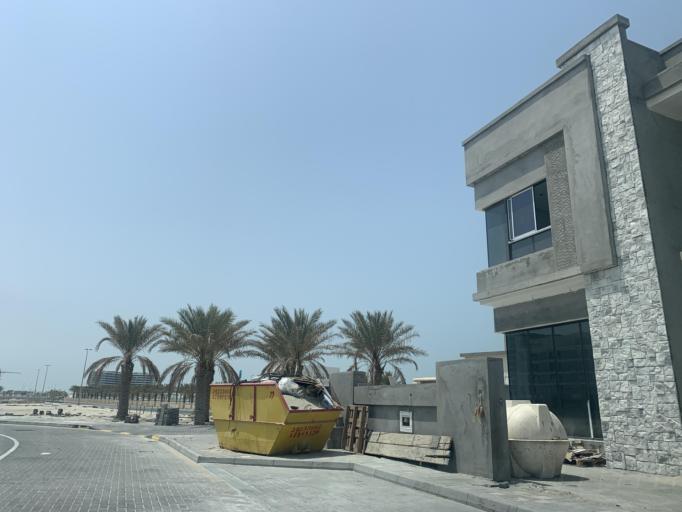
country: BH
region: Muharraq
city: Al Hadd
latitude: 26.2701
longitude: 50.6799
